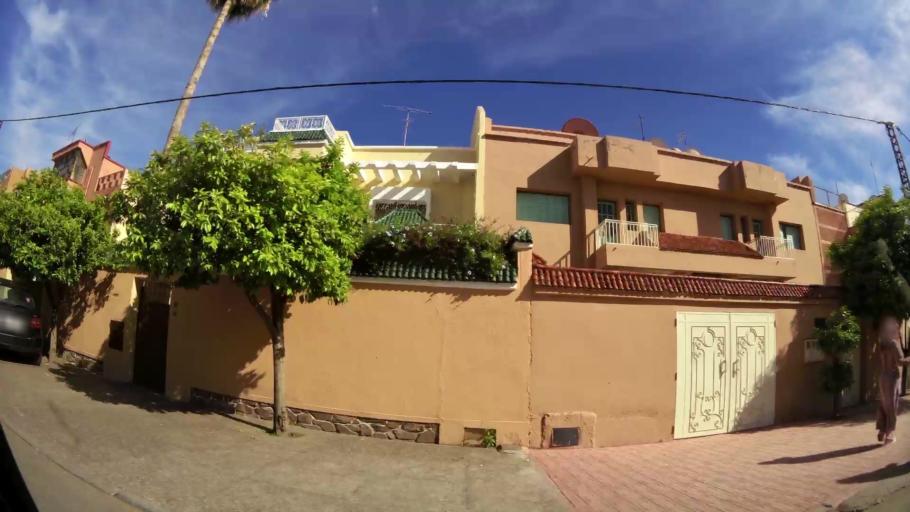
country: MA
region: Marrakech-Tensift-Al Haouz
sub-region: Marrakech
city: Marrakesh
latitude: 31.6462
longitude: -8.0065
